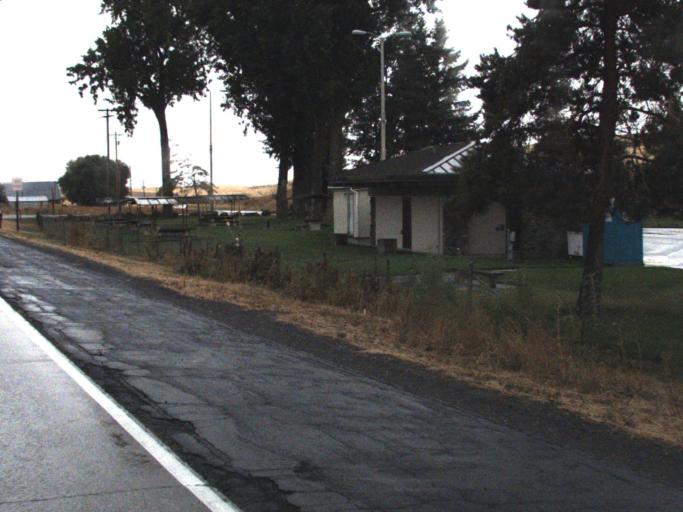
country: US
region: Washington
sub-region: Whitman County
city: Colfax
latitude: 47.1821
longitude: -117.3767
